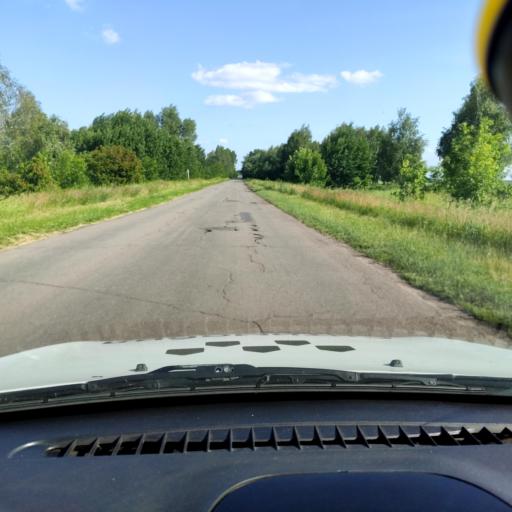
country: RU
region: Samara
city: Zhigulevsk
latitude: 53.3410
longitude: 49.3670
